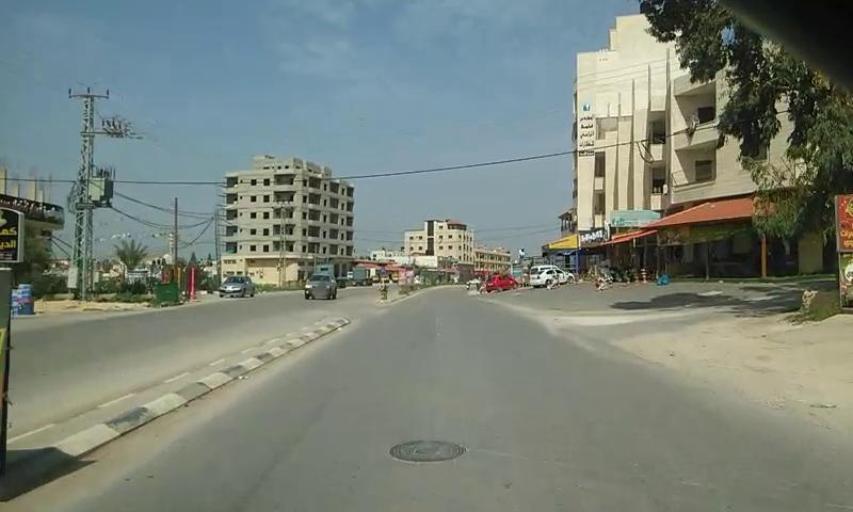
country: PS
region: West Bank
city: `Arranah
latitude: 32.4858
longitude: 35.2997
